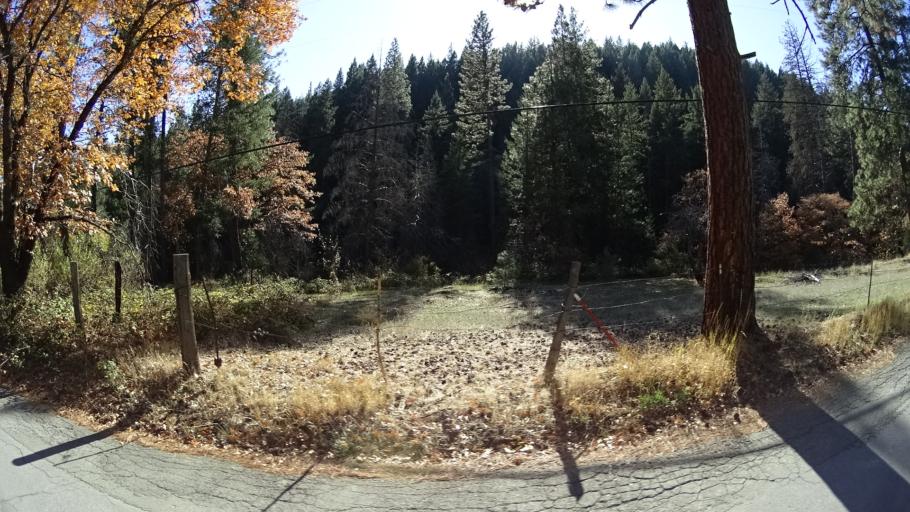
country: US
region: California
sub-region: Siskiyou County
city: Yreka
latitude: 41.7276
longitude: -122.7054
